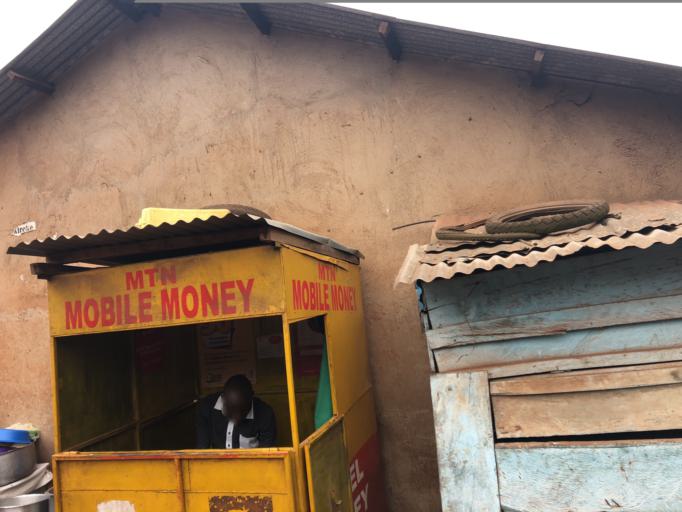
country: UG
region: Central Region
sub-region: Mukono District
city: Mukono
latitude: 0.3564
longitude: 32.7515
